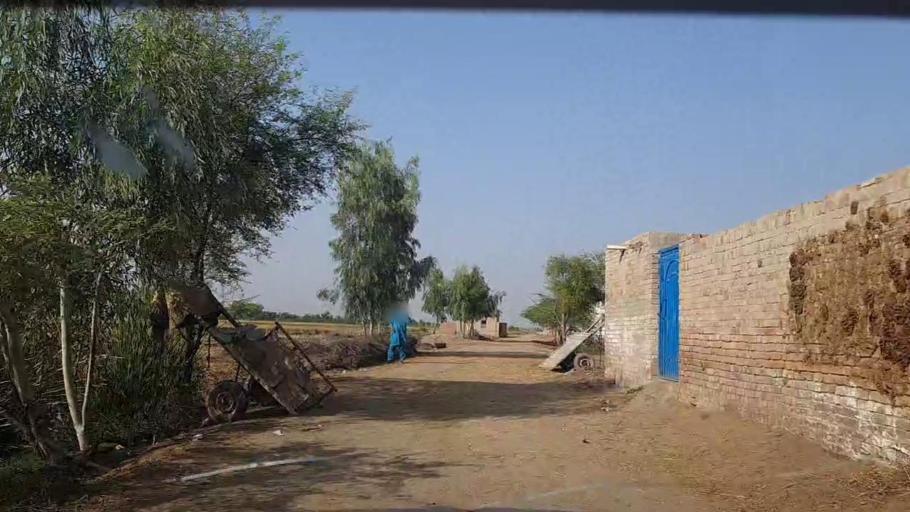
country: PK
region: Sindh
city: Shikarpur
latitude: 28.1213
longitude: 68.5786
